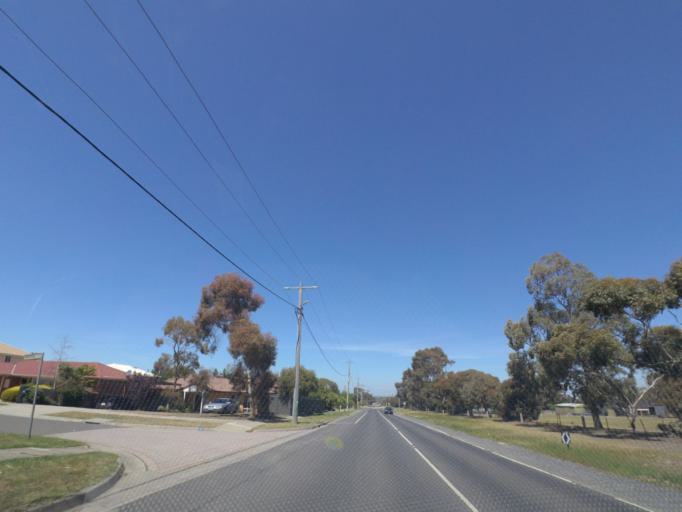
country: AU
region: Victoria
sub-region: Hume
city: Sunbury
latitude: -37.5747
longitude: 144.6941
